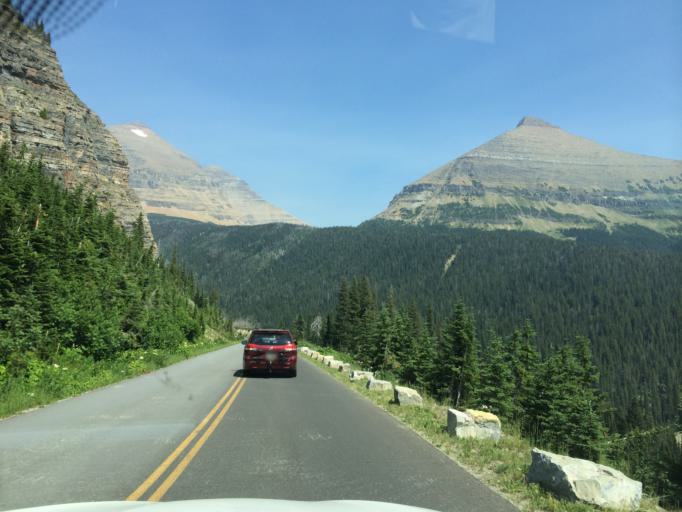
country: US
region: Montana
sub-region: Flathead County
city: Columbia Falls
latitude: 48.6942
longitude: -113.6751
